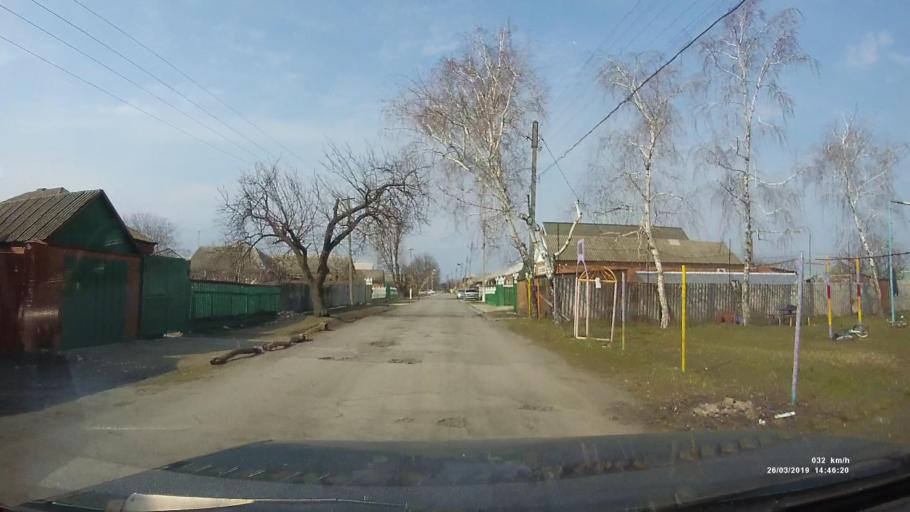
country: RU
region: Rostov
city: Novobessergenovka
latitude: 47.1861
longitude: 38.8606
